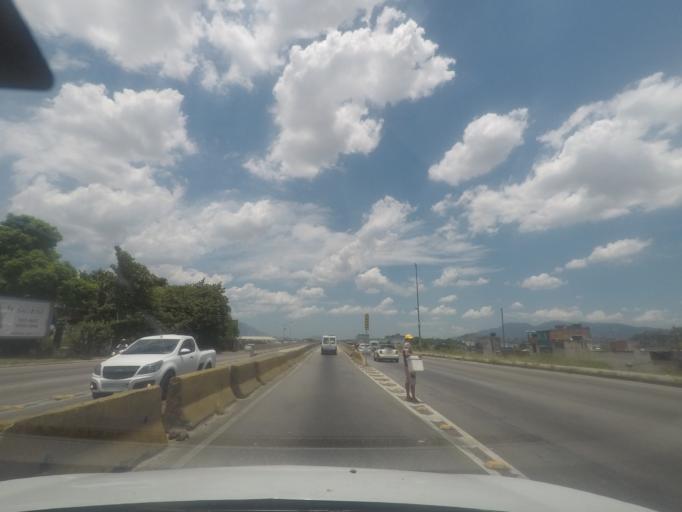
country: BR
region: Rio de Janeiro
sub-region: Sao Joao De Meriti
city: Sao Joao de Meriti
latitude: -22.8284
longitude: -43.3442
